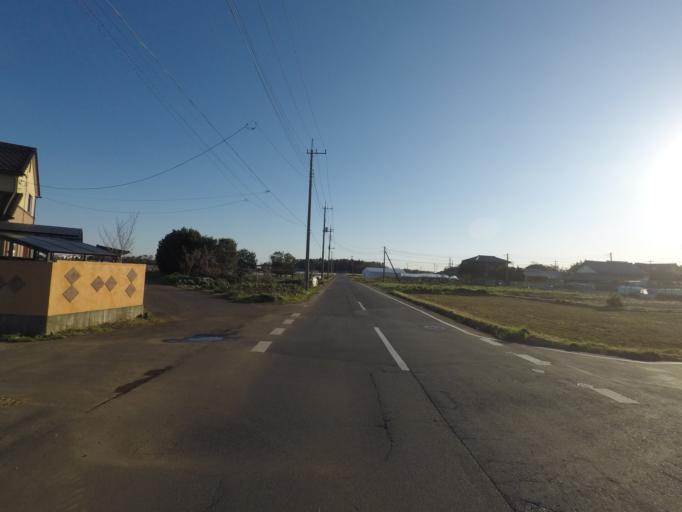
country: JP
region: Ibaraki
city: Ishige
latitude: 36.1221
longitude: 140.0283
